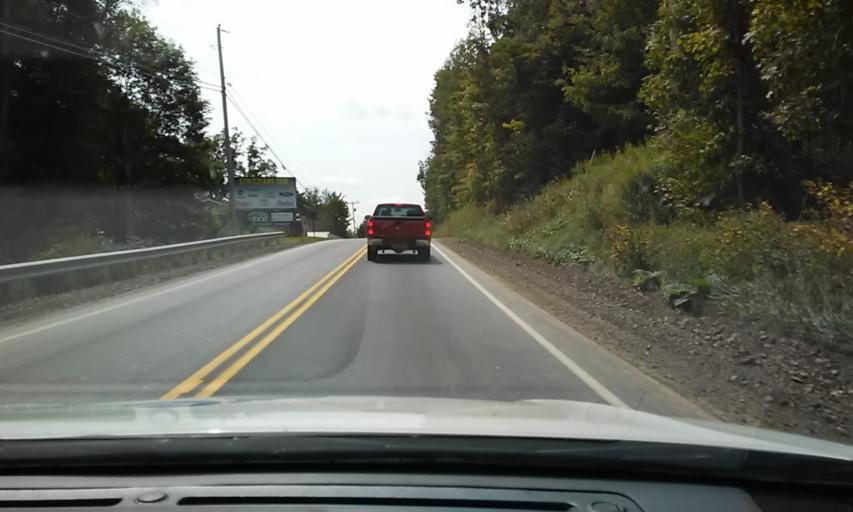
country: US
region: Pennsylvania
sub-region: Clearfield County
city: Treasure Lake
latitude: 41.1735
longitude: -78.6506
